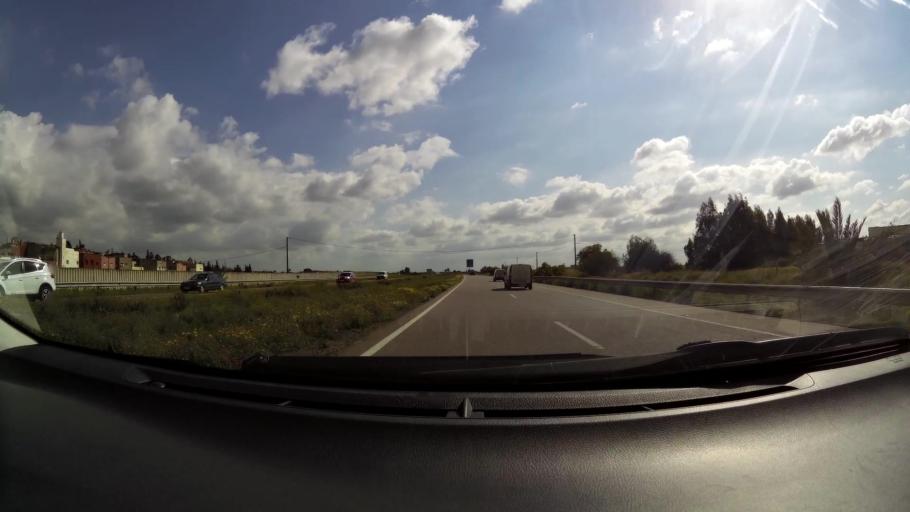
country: MA
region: Chaouia-Ouardigha
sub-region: Settat Province
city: Berrechid
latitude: 33.2598
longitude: -7.5563
